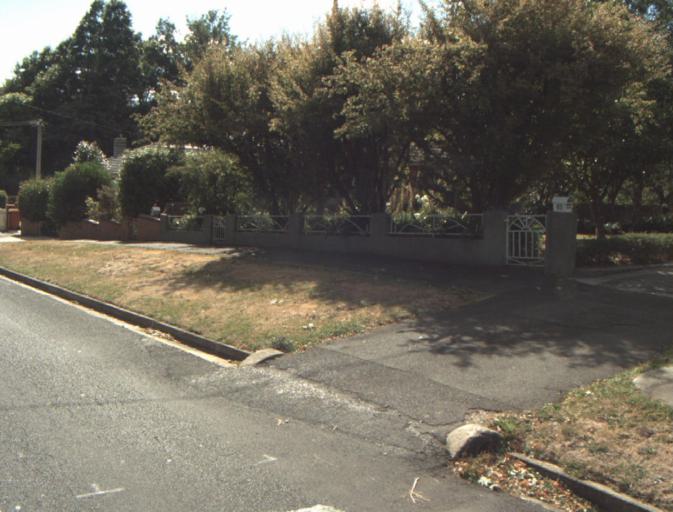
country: AU
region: Tasmania
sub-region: Launceston
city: East Launceston
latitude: -41.4504
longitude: 147.1610
